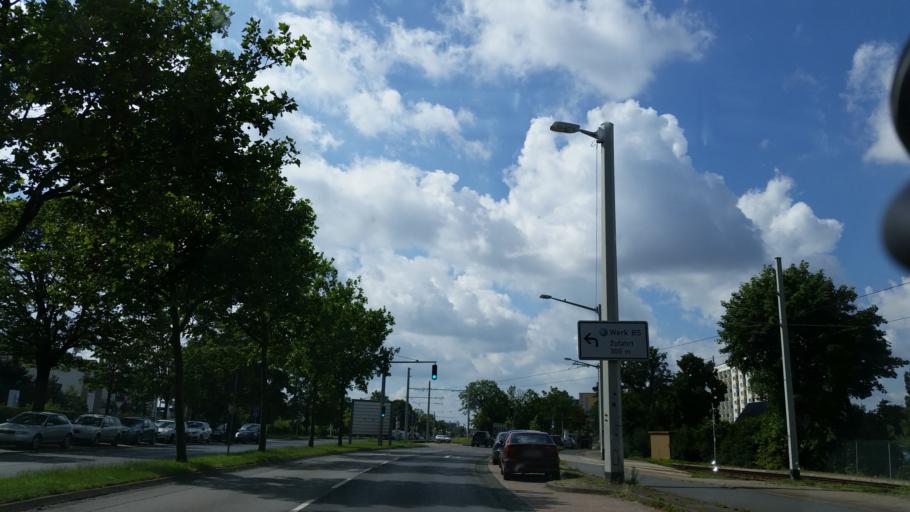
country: DE
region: Lower Saxony
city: Braunschweig
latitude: 52.2936
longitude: 10.5183
